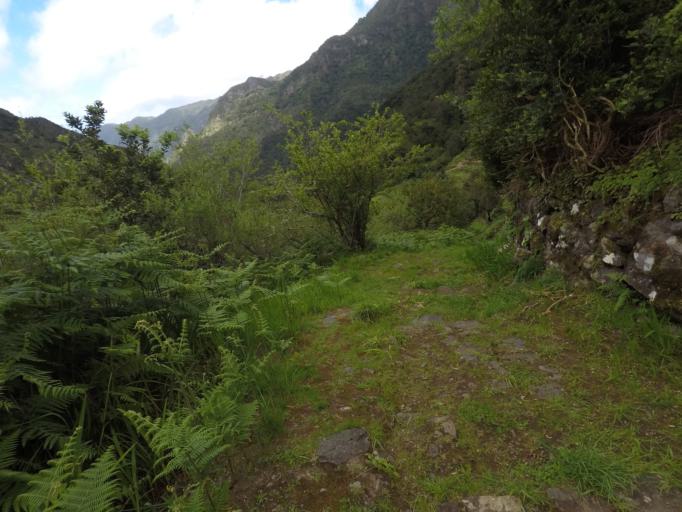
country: PT
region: Madeira
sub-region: Camara de Lobos
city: Curral das Freiras
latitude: 32.7797
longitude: -16.9805
